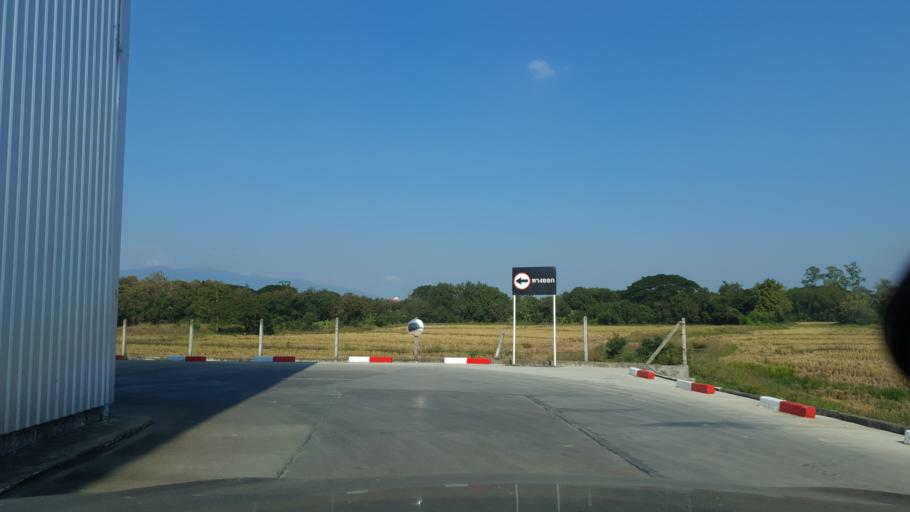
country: TH
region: Chiang Mai
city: Saraphi
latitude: 18.7222
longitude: 99.0442
